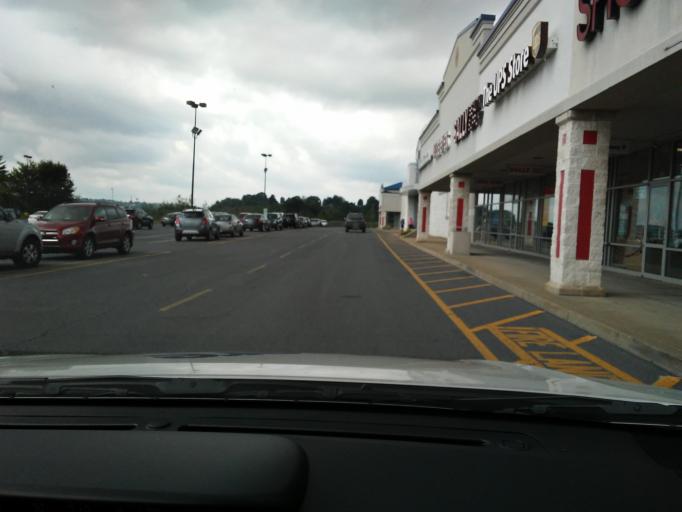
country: US
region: Pennsylvania
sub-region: Clearfield County
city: DuBois
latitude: 41.1263
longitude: -78.7334
